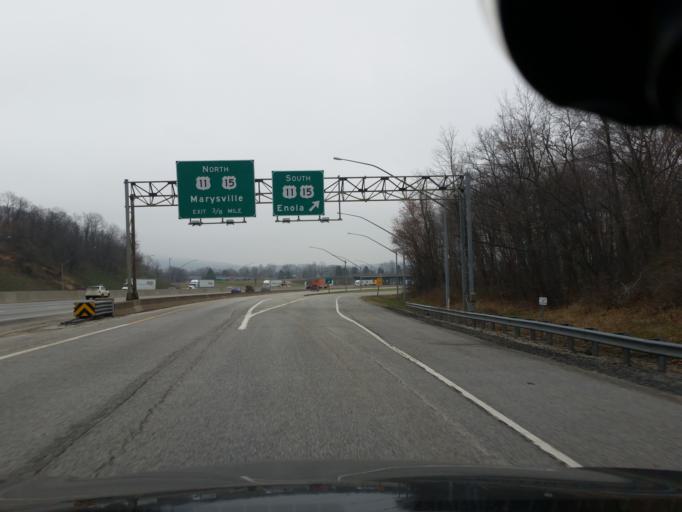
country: US
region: Pennsylvania
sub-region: Cumberland County
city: Enola
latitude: 40.3159
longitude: -76.9269
